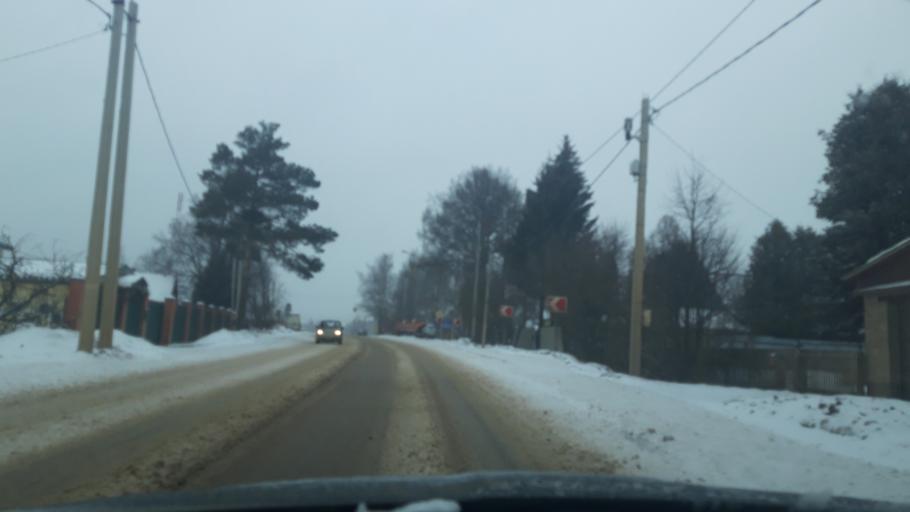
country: RU
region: Moskovskaya
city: Avtopoligon
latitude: 56.2561
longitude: 37.2286
